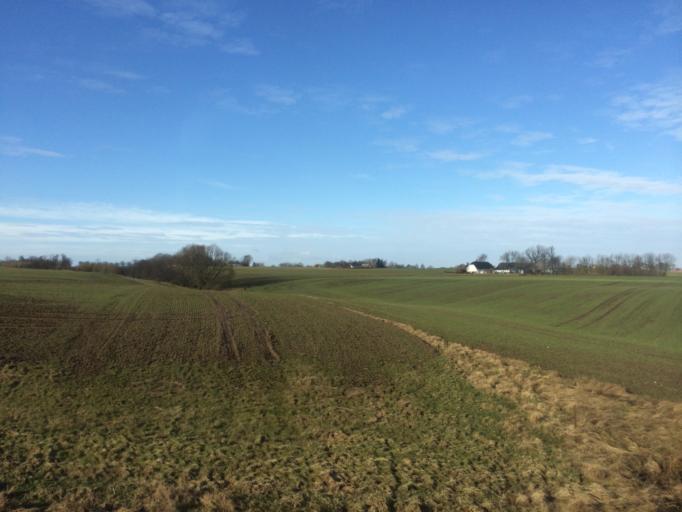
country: DK
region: South Denmark
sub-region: Vejle Kommune
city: Jelling
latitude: 55.7661
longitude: 9.4475
